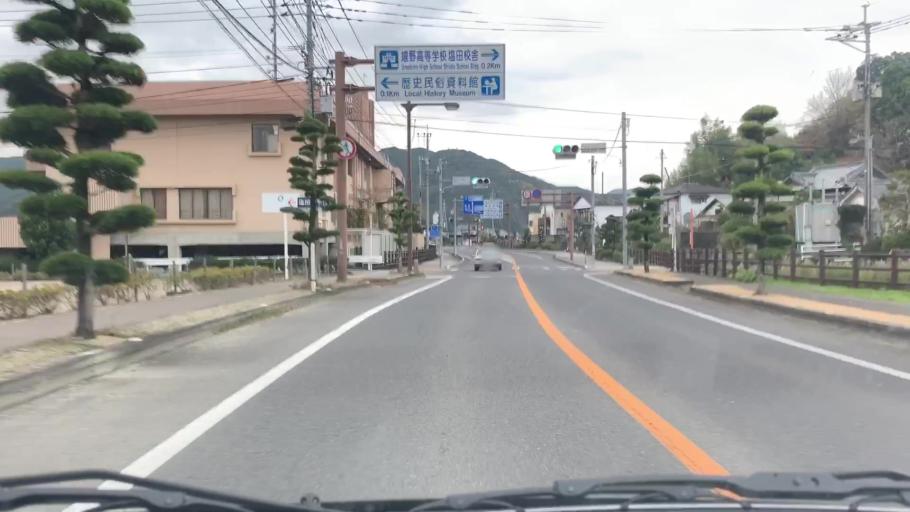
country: JP
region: Saga Prefecture
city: Kashima
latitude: 33.1290
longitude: 130.0601
